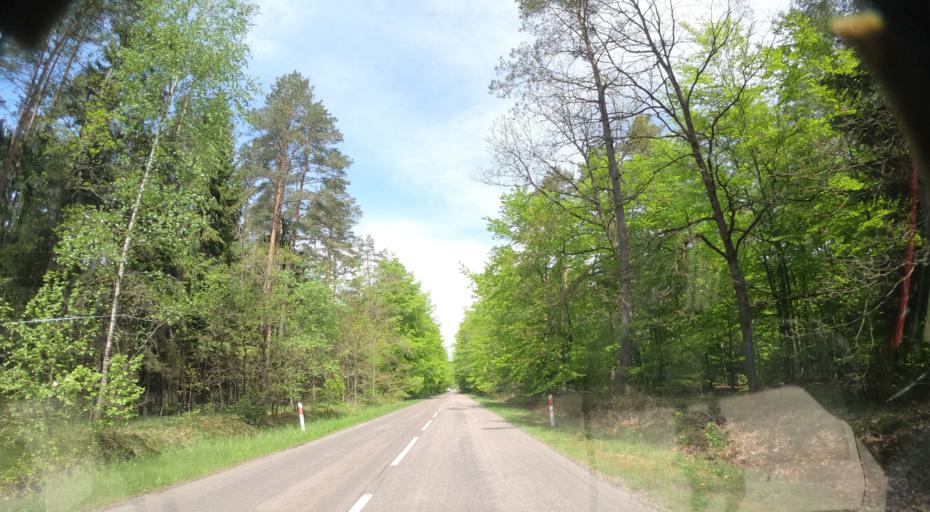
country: PL
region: West Pomeranian Voivodeship
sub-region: Powiat bialogardzki
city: Tychowo
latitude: 54.0591
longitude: 16.3011
